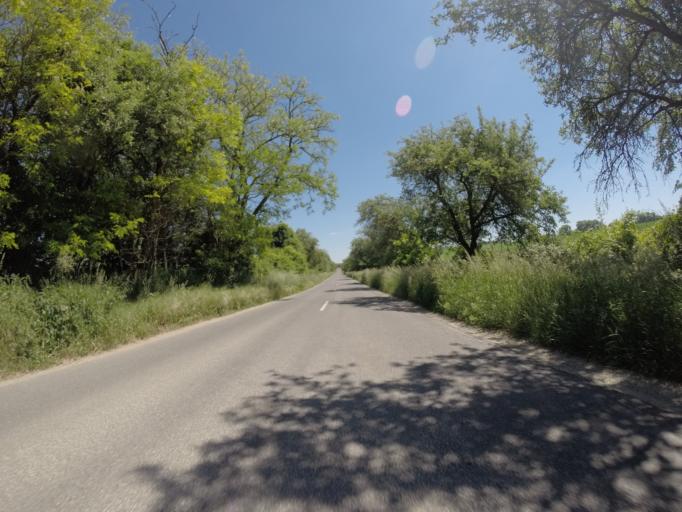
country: SK
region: Trnavsky
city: Hlohovec
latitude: 48.4736
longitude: 17.8956
